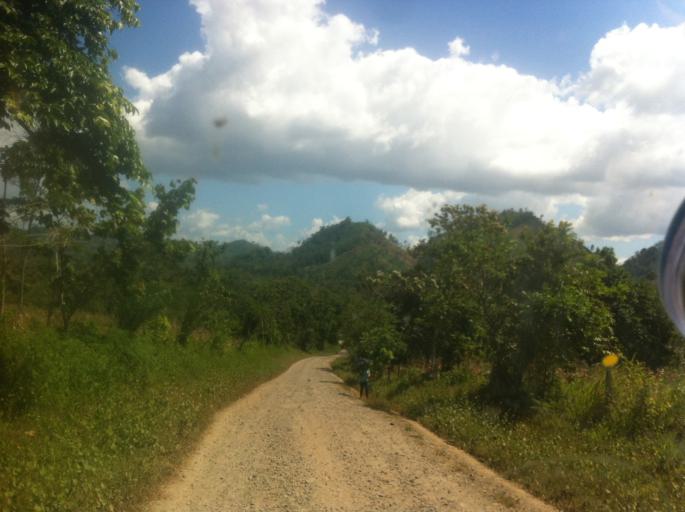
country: CR
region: Alajuela
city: Los Chiles
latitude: 11.2379
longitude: -84.5102
